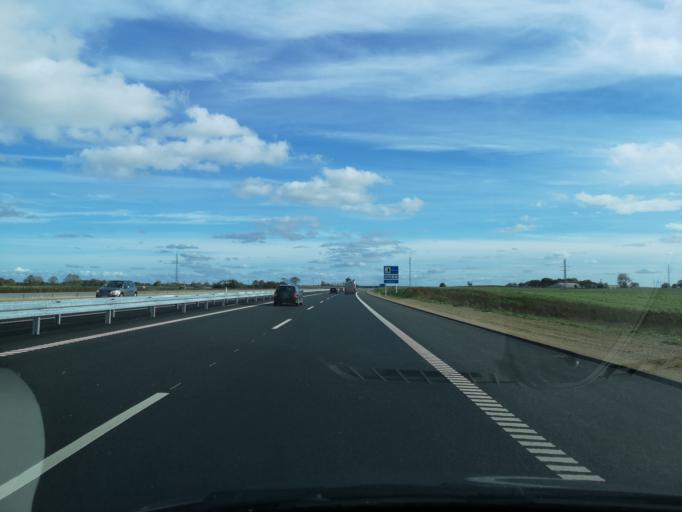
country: DK
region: Central Jutland
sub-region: Holstebro Kommune
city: Holstebro
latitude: 56.3771
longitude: 8.6966
